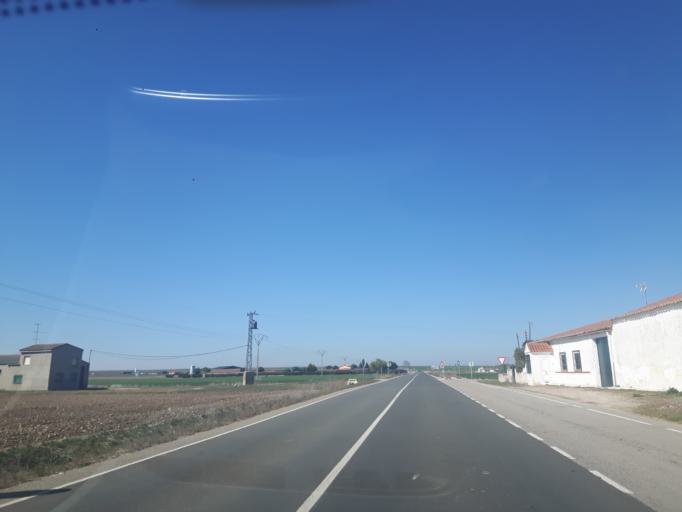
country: ES
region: Castille and Leon
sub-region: Provincia de Salamanca
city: Nava de Sotrobal
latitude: 40.8875
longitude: -5.2810
